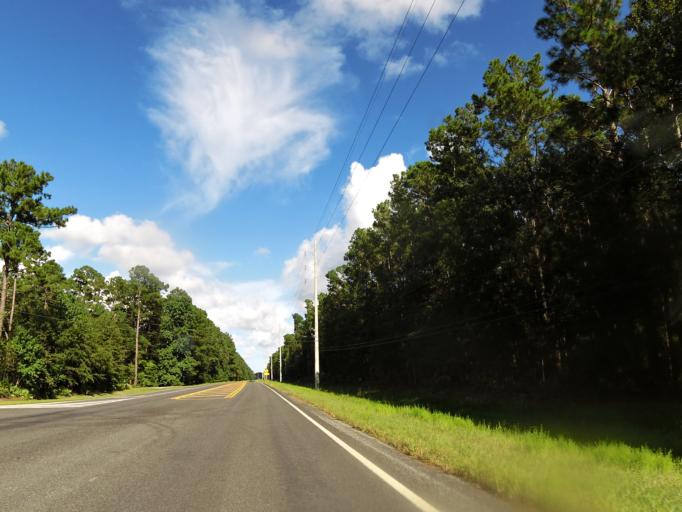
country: US
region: Georgia
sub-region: Glynn County
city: Brunswick
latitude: 31.1064
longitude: -81.6458
